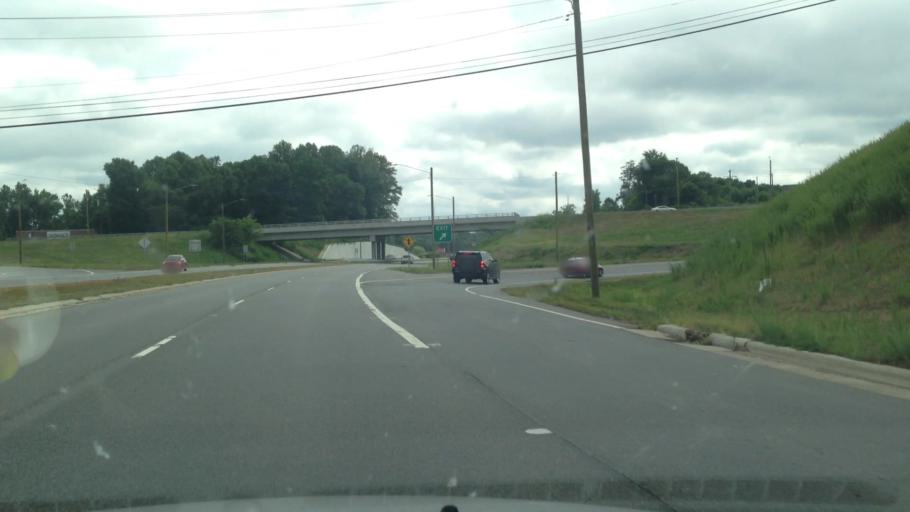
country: US
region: North Carolina
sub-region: Rockingham County
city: Reidsville
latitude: 36.3778
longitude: -79.6695
